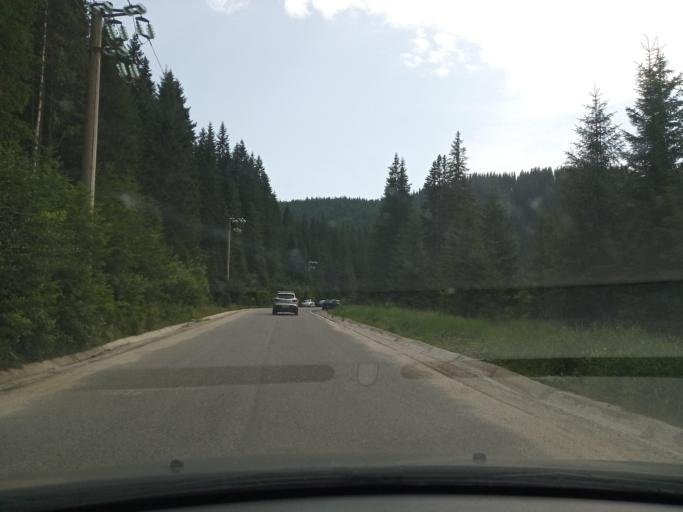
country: RO
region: Dambovita
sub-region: Comuna Moroeni
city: Glod
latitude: 45.3326
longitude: 25.4297
